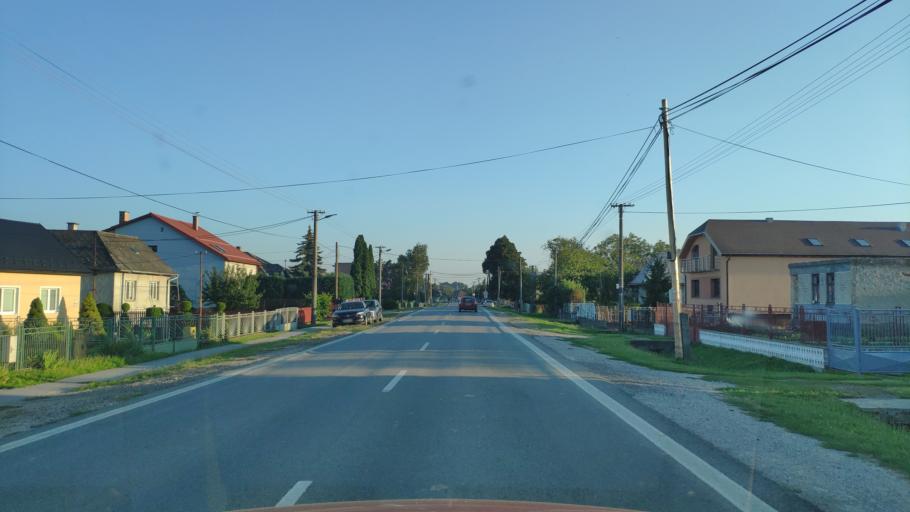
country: SK
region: Kosicky
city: Secovce
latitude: 48.7908
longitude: 21.6813
